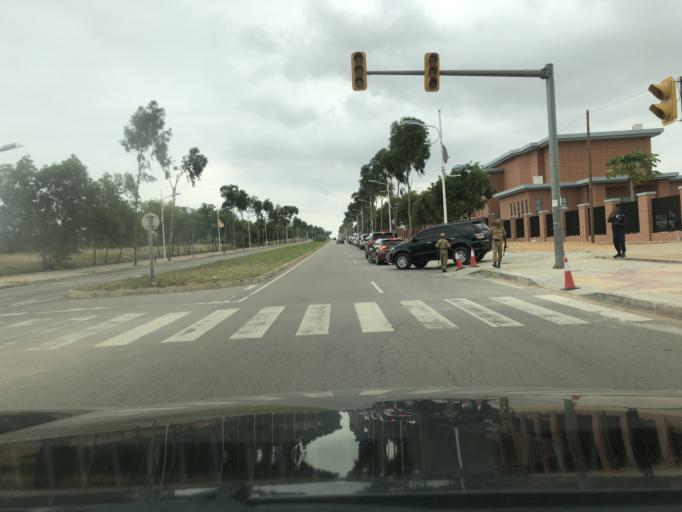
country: AO
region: Luanda
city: Luanda
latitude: -8.9912
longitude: 13.2844
